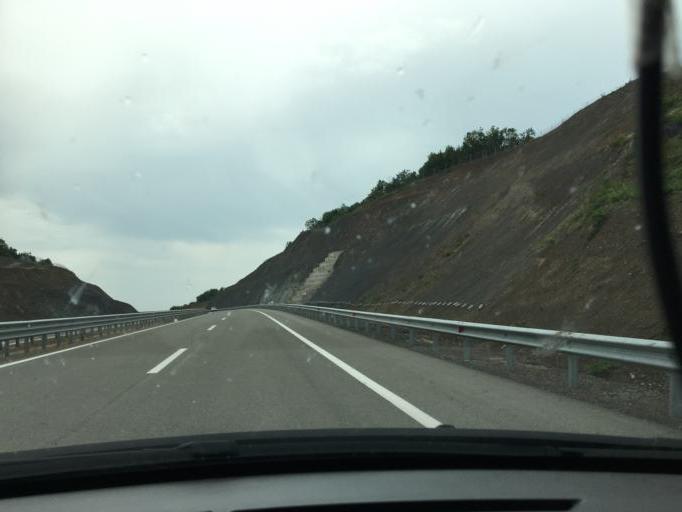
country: MK
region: Gevgelija
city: Miravci
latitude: 41.3400
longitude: 22.3792
